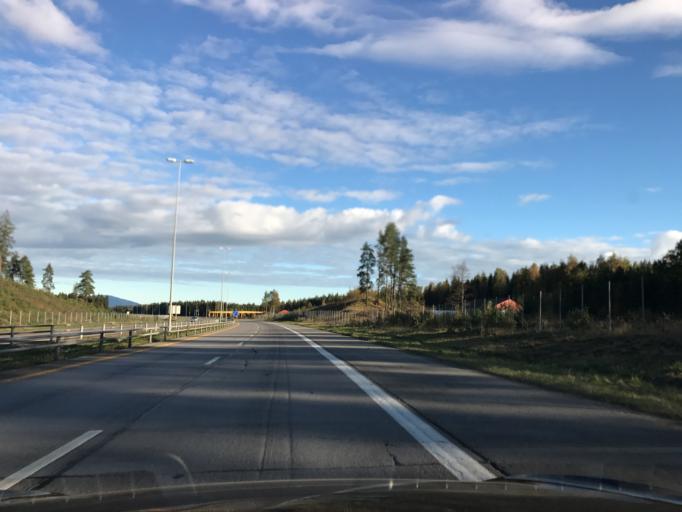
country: NO
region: Akershus
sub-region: Ullensaker
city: Jessheim
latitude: 60.1919
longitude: 11.1895
